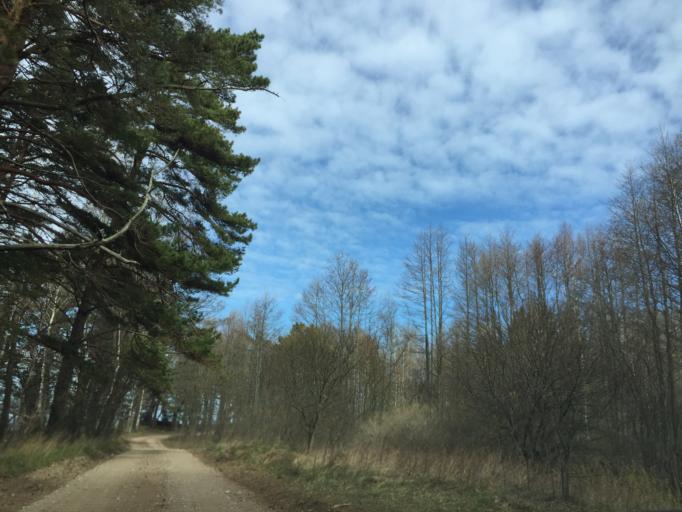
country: LV
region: Salacgrivas
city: Salacgriva
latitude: 57.5992
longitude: 24.3736
